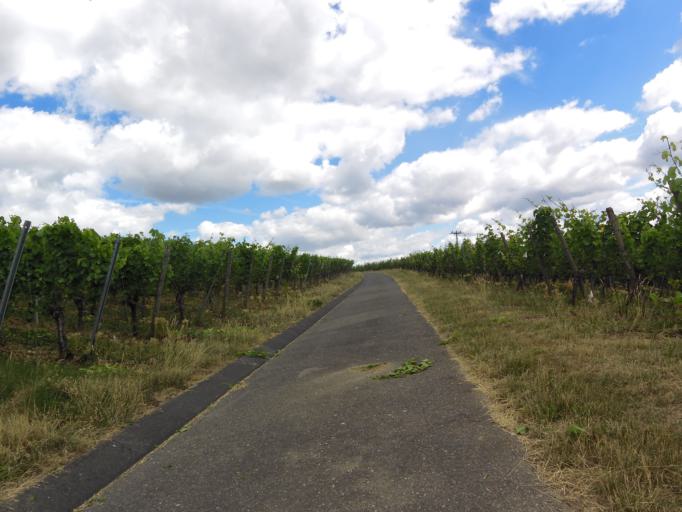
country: DE
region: Bavaria
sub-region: Regierungsbezirk Unterfranken
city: Gadheim
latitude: 49.8117
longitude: 9.9104
